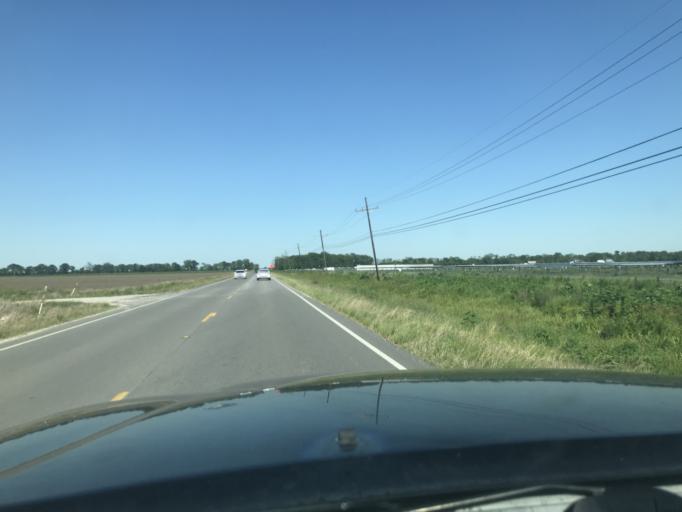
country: US
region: Louisiana
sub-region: West Baton Rouge Parish
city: Erwinville
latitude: 30.4687
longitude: -91.3329
